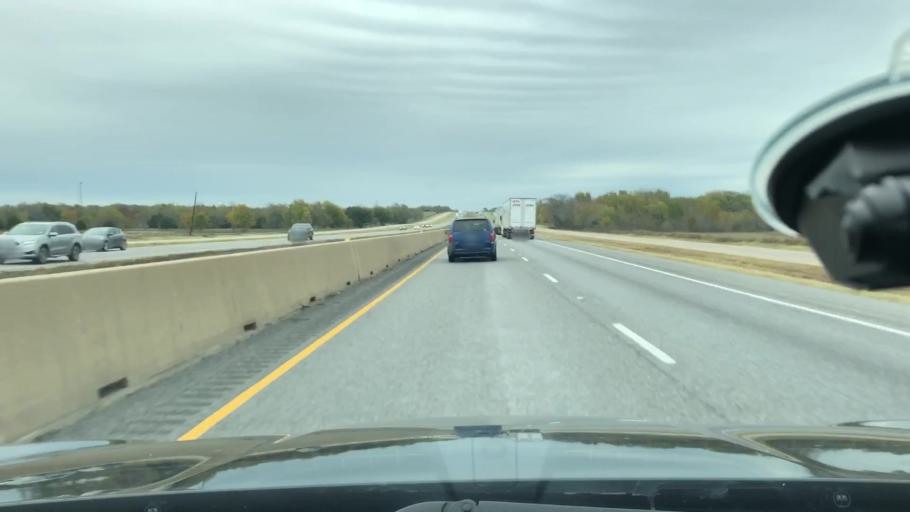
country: US
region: Texas
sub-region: Hunt County
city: Commerce
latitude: 33.1296
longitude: -95.8700
